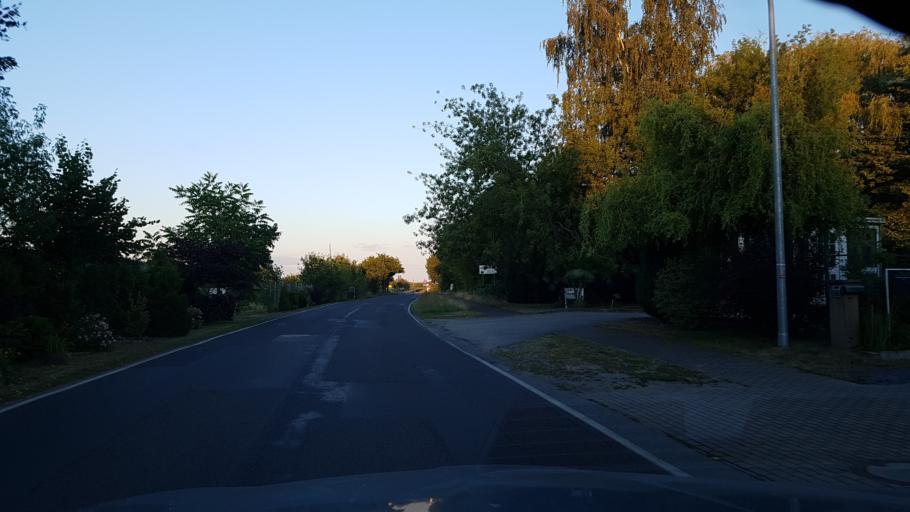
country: DE
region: Brandenburg
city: Groden
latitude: 51.4017
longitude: 13.5808
